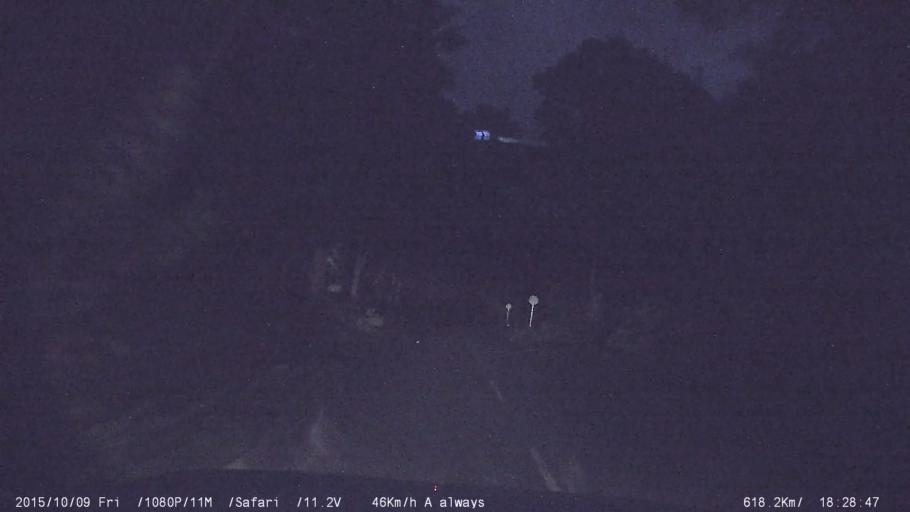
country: IN
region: Kerala
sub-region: Kottayam
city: Palackattumala
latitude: 9.7831
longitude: 76.6065
